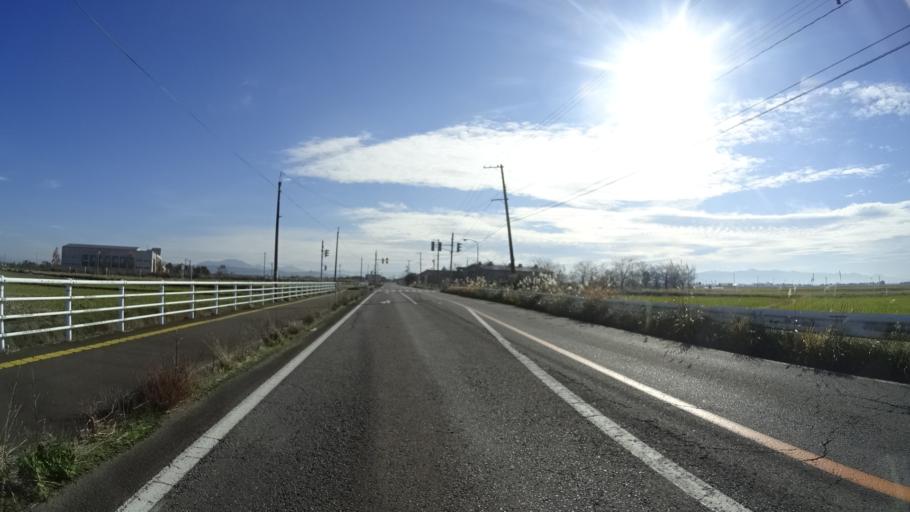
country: JP
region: Niigata
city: Mitsuke
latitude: 37.5538
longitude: 138.8593
